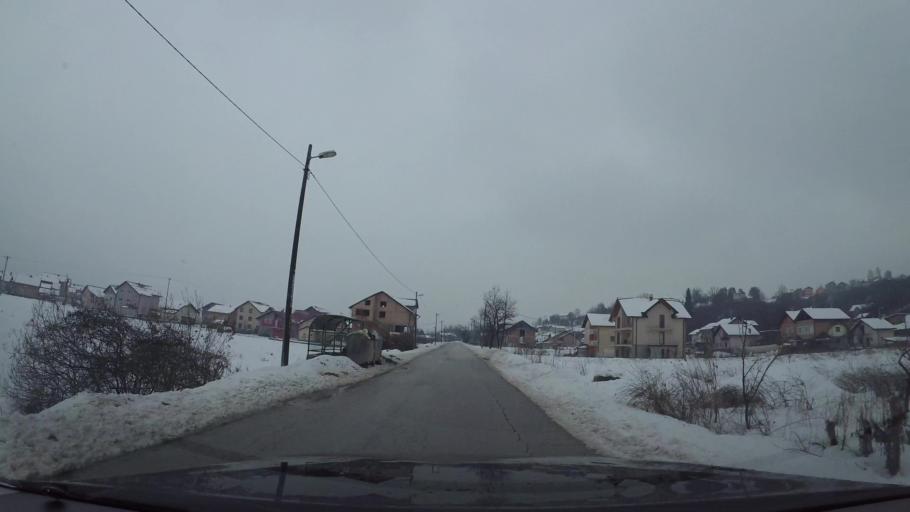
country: BA
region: Federation of Bosnia and Herzegovina
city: Hadzici
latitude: 43.8543
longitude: 18.2741
